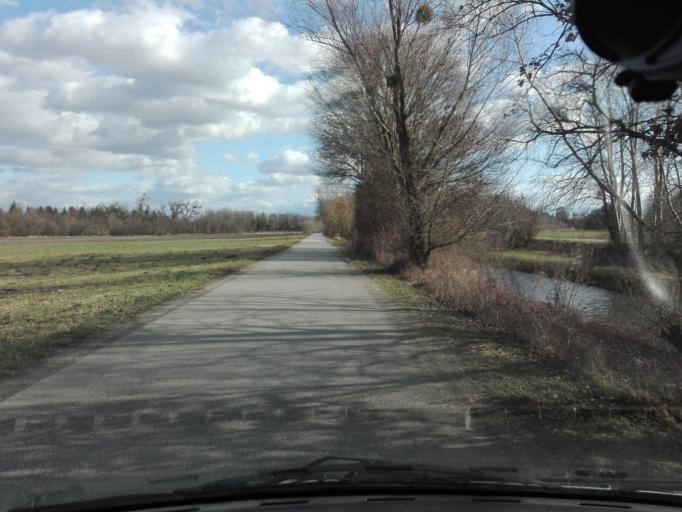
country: AT
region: Upper Austria
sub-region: Politischer Bezirk Perg
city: Perg
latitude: 48.2316
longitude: 14.6482
